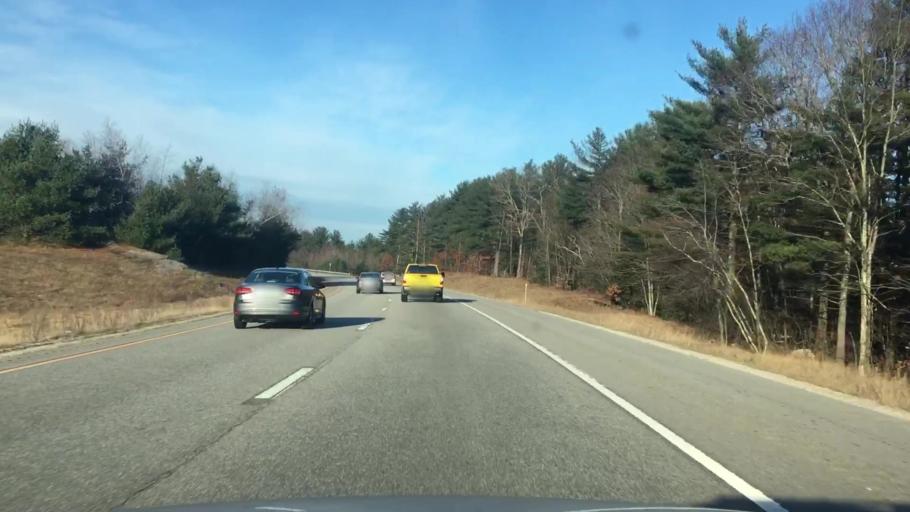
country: US
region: New Hampshire
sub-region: Rockingham County
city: Candia
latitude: 43.0425
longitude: -71.2677
